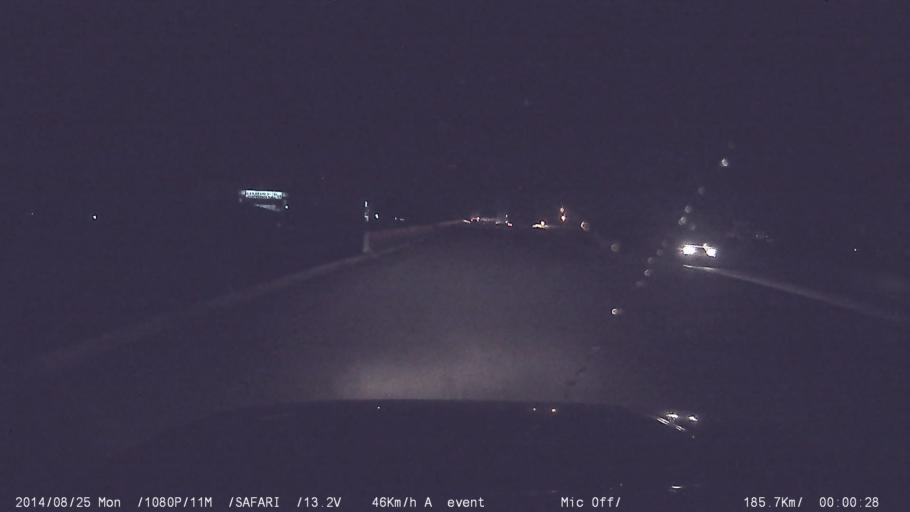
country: IN
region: Tamil Nadu
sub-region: Krishnagiri
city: Krishnagiri
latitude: 12.5115
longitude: 78.2190
